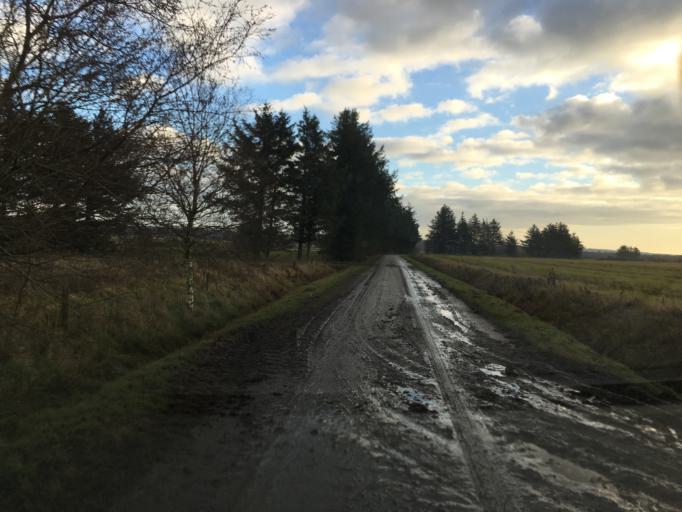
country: DK
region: South Denmark
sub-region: Tonder Kommune
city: Sherrebek
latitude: 55.1345
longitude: 8.8377
